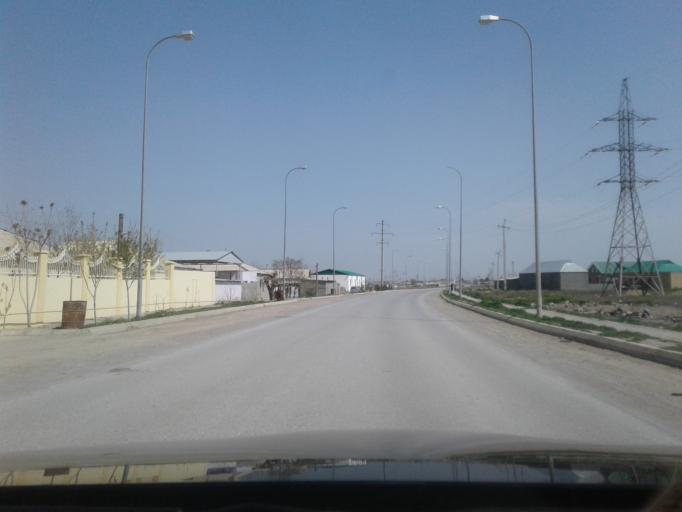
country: TM
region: Ahal
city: Abadan
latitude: 38.1604
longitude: 57.9785
